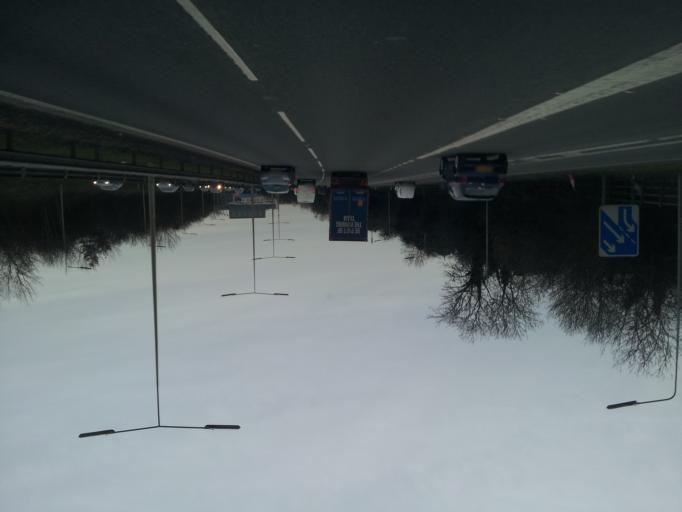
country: GB
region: England
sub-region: Hertfordshire
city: Hatfield
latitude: 51.7559
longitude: -0.2449
